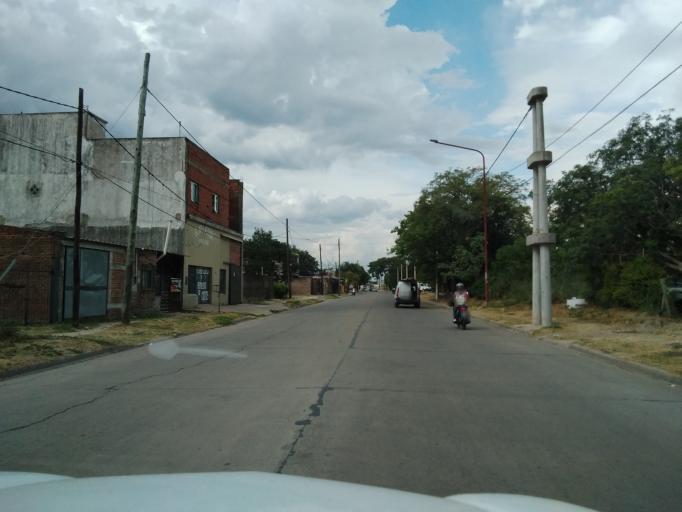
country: AR
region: Corrientes
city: Corrientes
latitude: -27.5247
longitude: -58.7956
